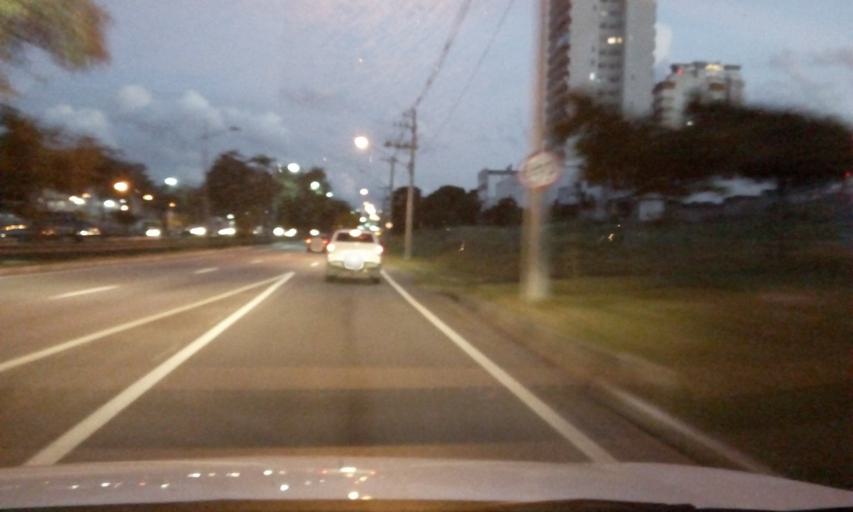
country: BR
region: Sao Paulo
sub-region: Sao Jose Dos Campos
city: Sao Jose dos Campos
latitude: -23.2135
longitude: -45.8905
